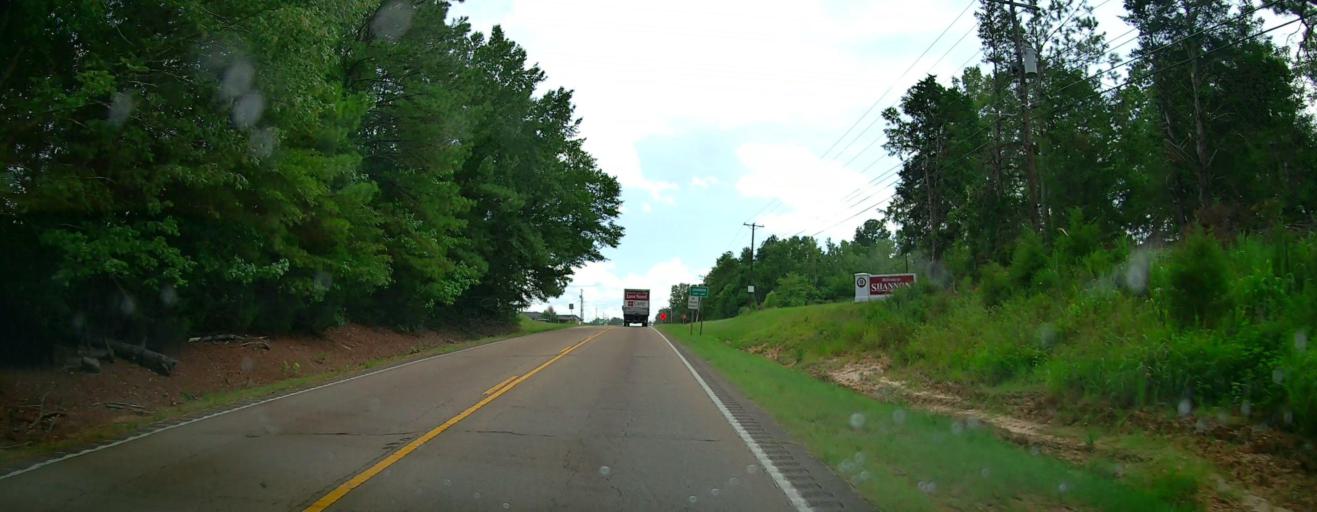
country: US
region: Mississippi
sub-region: Lee County
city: Shannon
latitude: 34.1324
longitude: -88.7194
